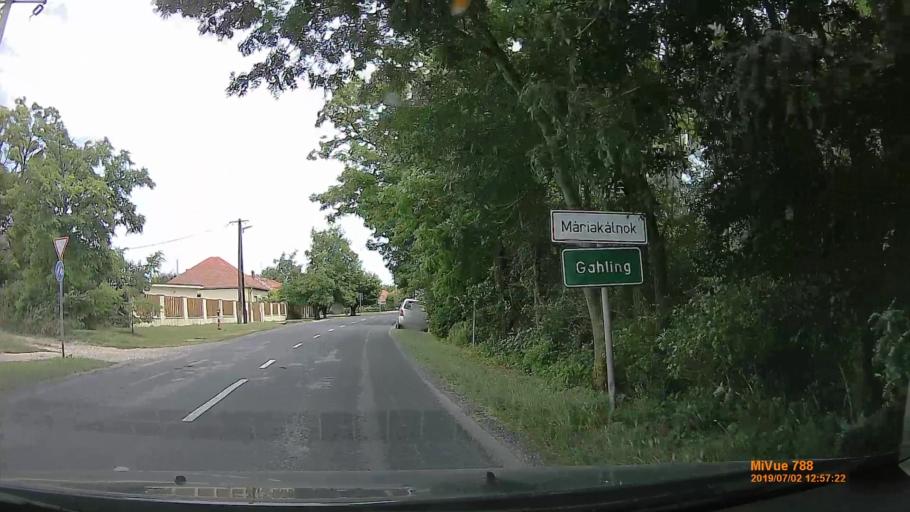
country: HU
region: Gyor-Moson-Sopron
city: Halaszi
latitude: 47.8559
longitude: 17.3099
